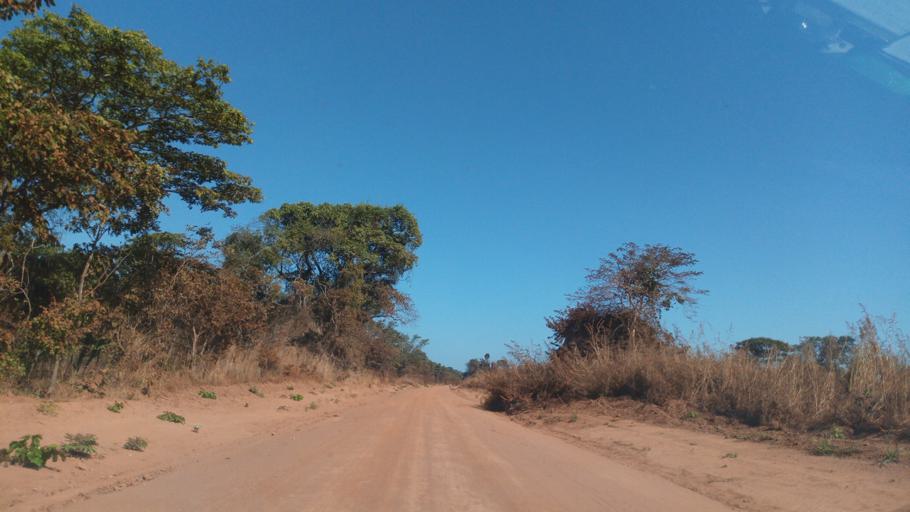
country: ZM
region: Luapula
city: Mwense
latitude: -10.7548
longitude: 28.3171
